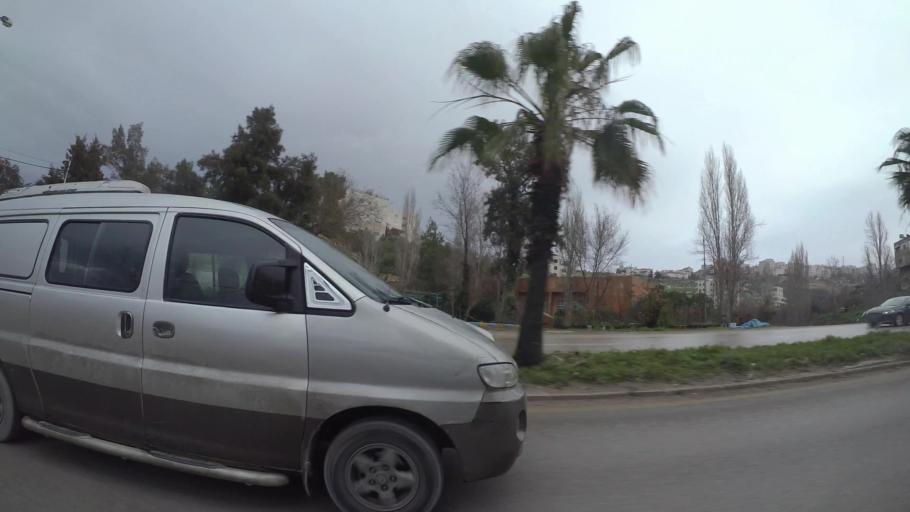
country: JO
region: Amman
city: Al Jubayhah
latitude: 32.0400
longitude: 35.8369
